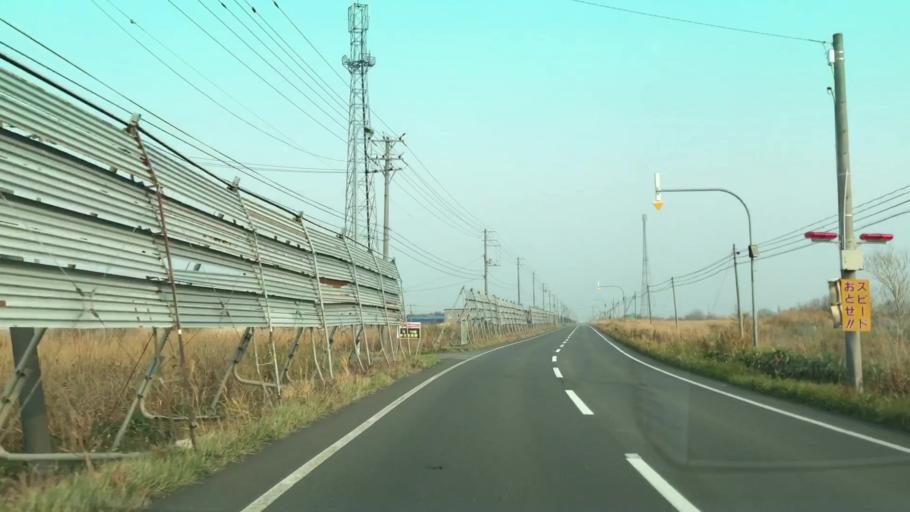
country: JP
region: Hokkaido
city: Ishikari
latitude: 43.2874
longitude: 141.4096
